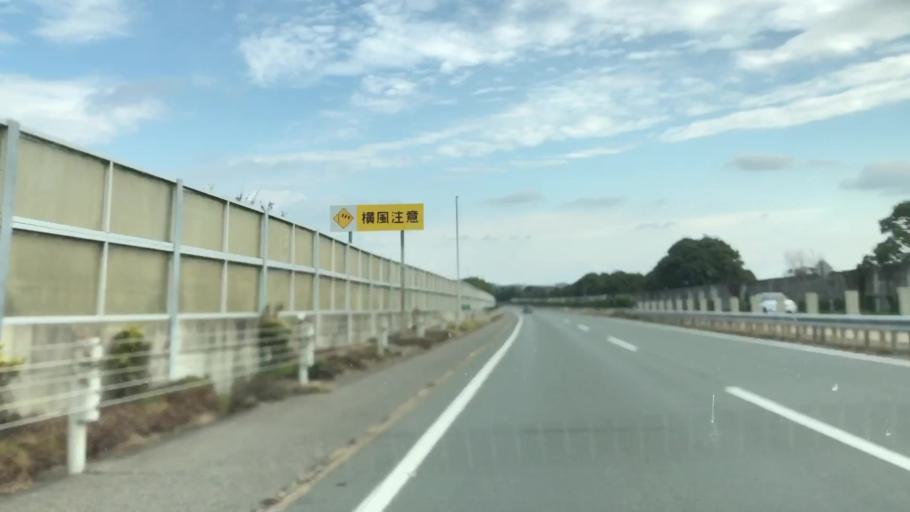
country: JP
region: Saga Prefecture
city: Kanzakimachi-kanzaki
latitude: 33.3288
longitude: 130.3034
